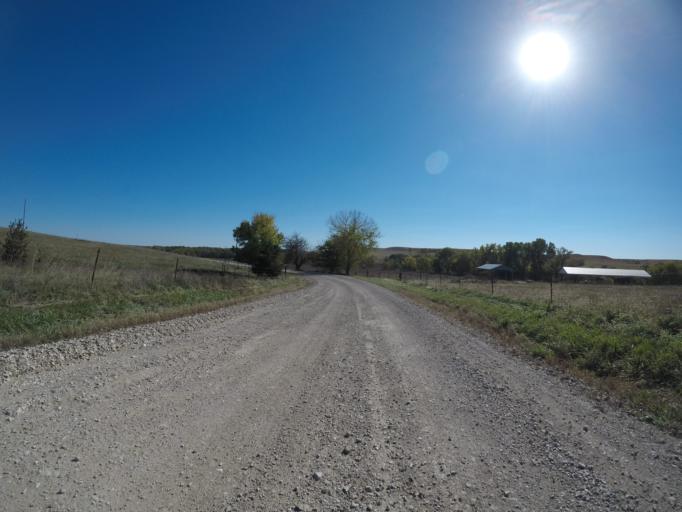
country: US
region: Kansas
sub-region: Wabaunsee County
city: Alma
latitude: 38.9434
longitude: -96.4364
